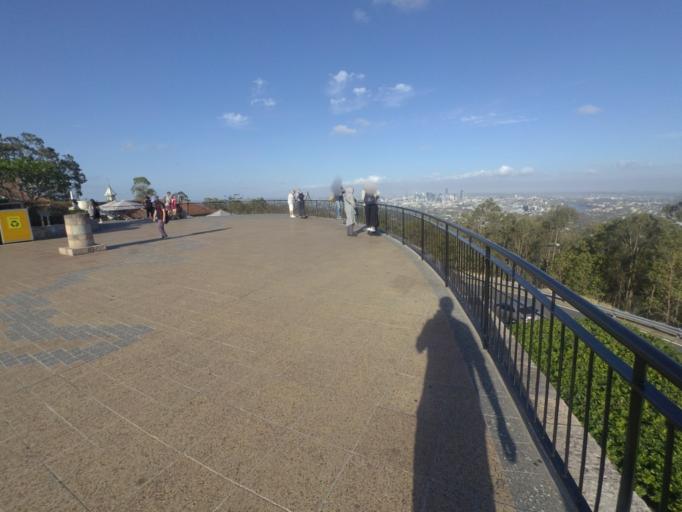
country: AU
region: Queensland
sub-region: Brisbane
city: Taringa
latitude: -27.4852
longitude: 152.9591
